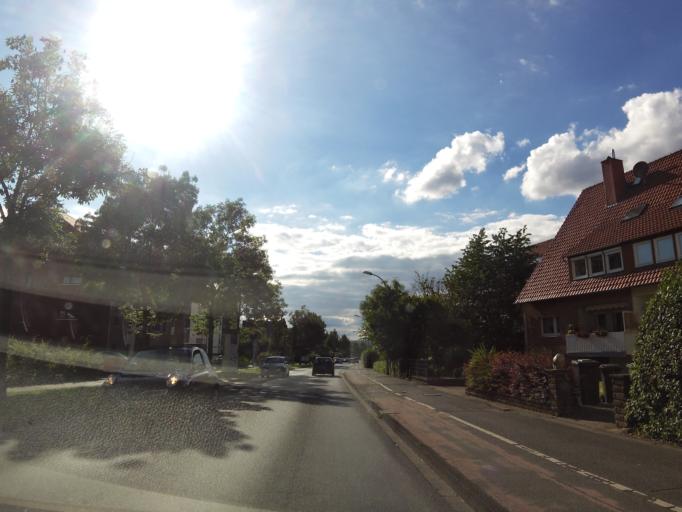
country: DE
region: Lower Saxony
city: Goettingen
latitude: 51.5127
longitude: 9.9443
